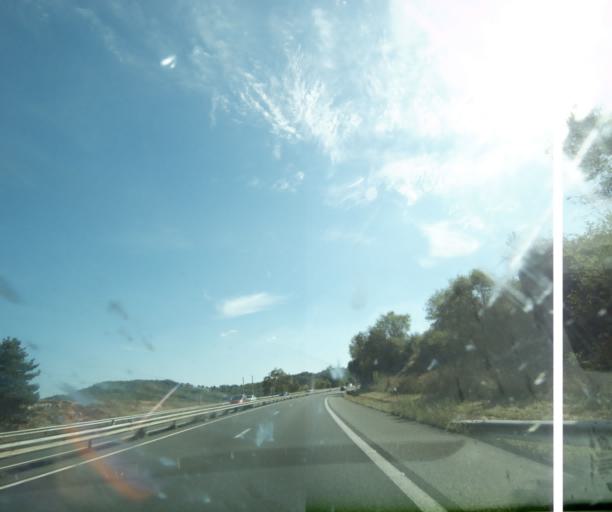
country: FR
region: Limousin
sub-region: Departement de la Correze
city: Brive-la-Gaillarde
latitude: 45.1206
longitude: 1.5005
